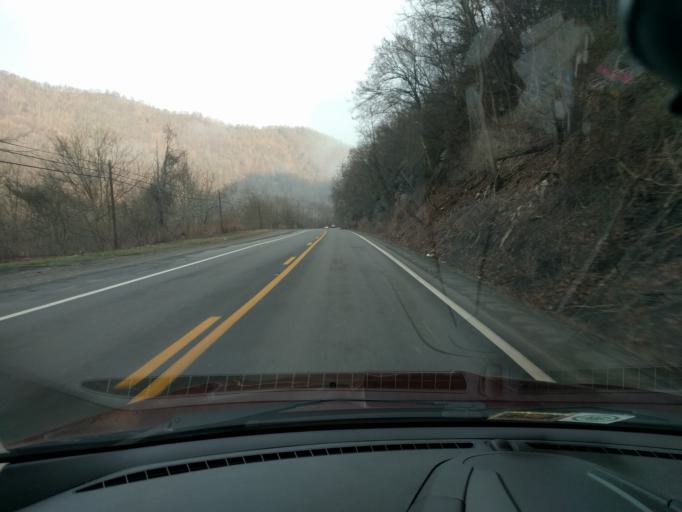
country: US
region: West Virginia
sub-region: Kanawha County
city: Montgomery
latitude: 38.1603
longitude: -81.2983
